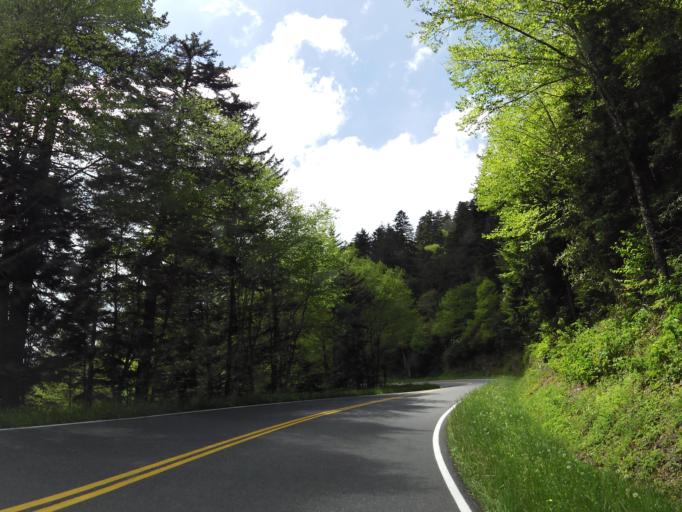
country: US
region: Tennessee
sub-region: Sevier County
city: Gatlinburg
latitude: 35.6090
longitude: -83.4403
